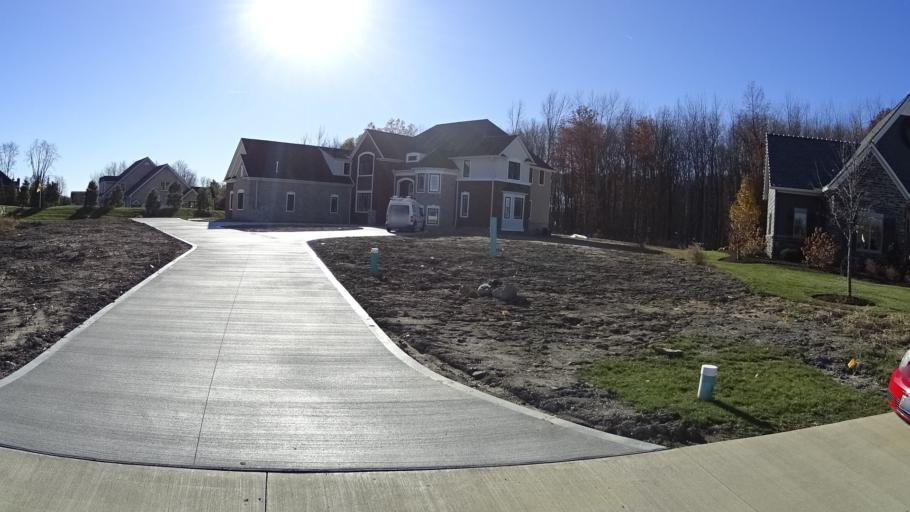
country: US
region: Ohio
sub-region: Lorain County
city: Avon Center
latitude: 41.4365
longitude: -81.9905
